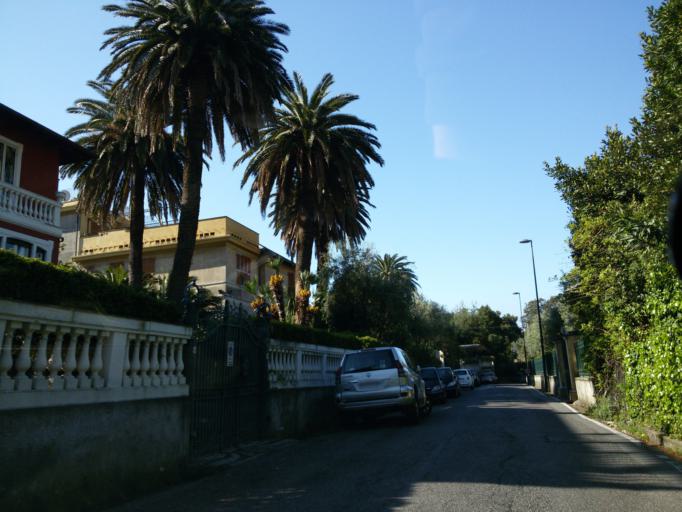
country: IT
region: Liguria
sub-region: Provincia di Genova
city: Bogliasco
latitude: 44.3898
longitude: 9.0056
